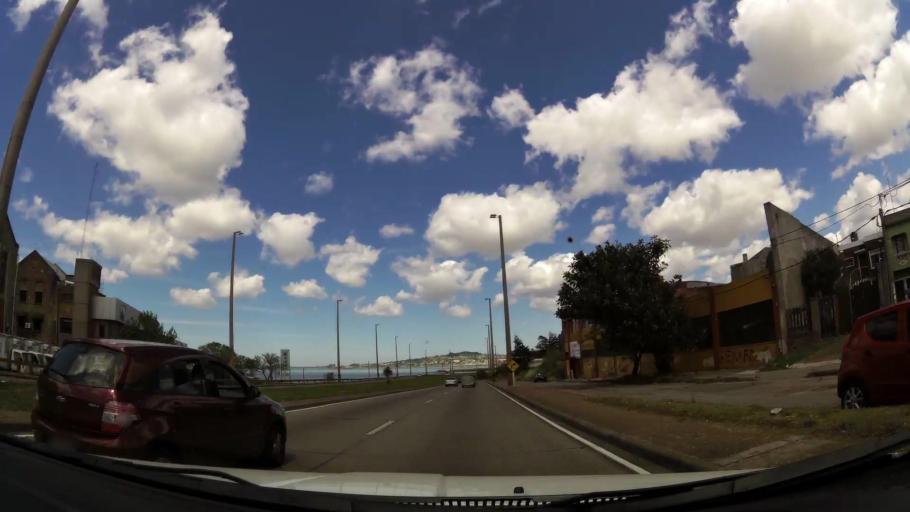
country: UY
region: Montevideo
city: Montevideo
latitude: -34.8739
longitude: -56.2084
